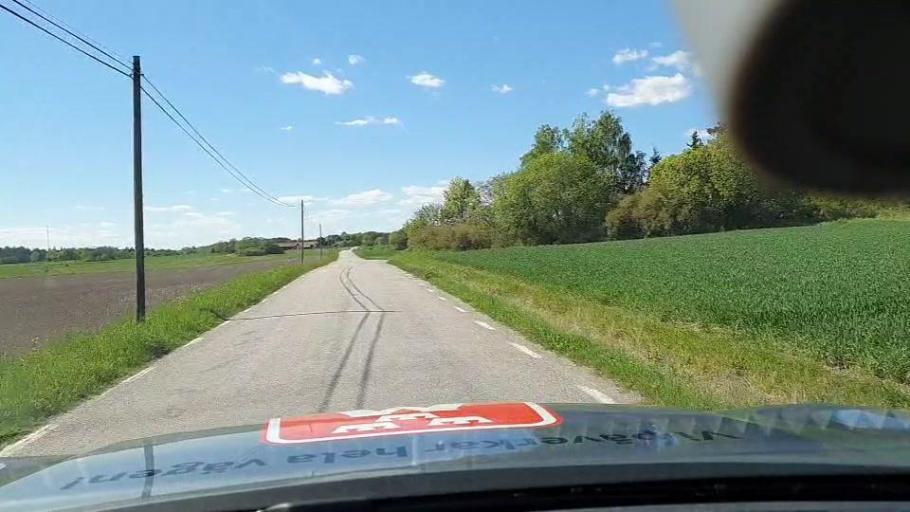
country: SE
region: Soedermanland
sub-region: Strangnas Kommun
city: Strangnas
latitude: 59.4498
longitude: 16.8723
